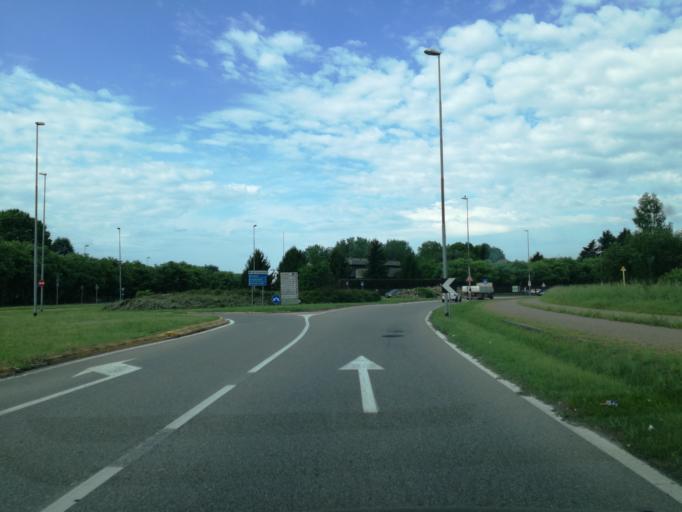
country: IT
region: Lombardy
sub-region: Provincia di Monza e Brianza
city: Giussano
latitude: 45.6896
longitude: 9.2085
